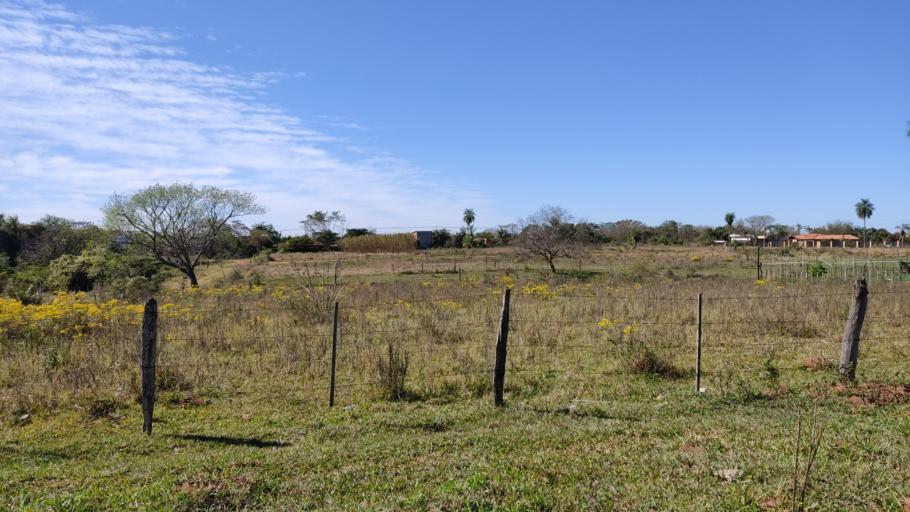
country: PY
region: Misiones
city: San Juan Bautista
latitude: -26.6746
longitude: -57.1413
